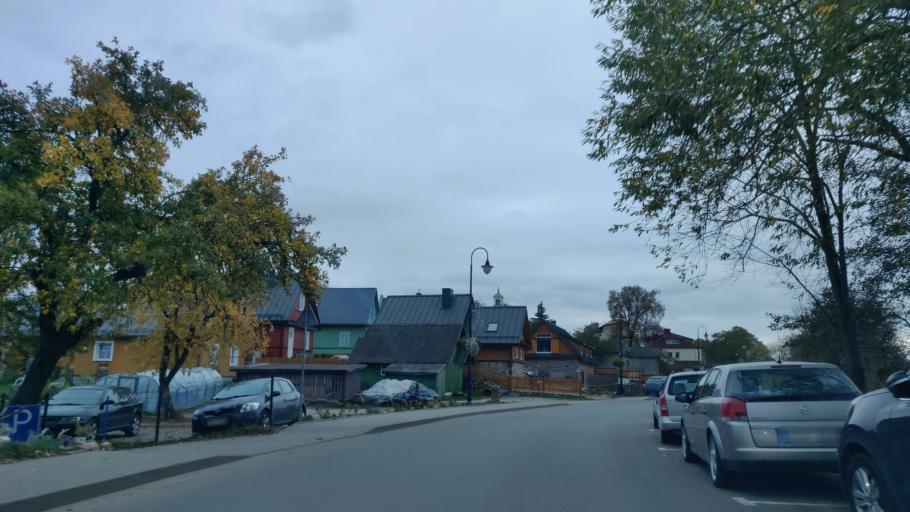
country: LT
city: Trakai
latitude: 54.6488
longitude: 24.9314
